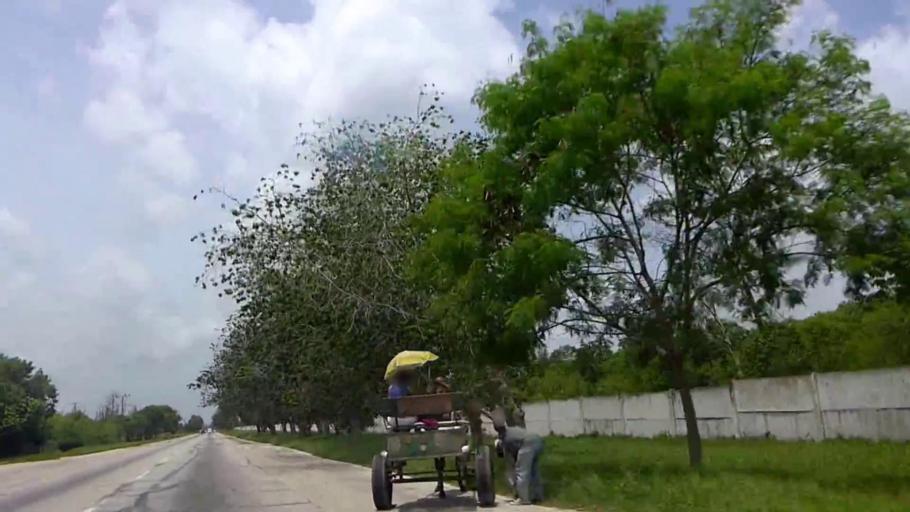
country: CU
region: Holguin
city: Cacocum
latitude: 20.7953
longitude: -76.2982
